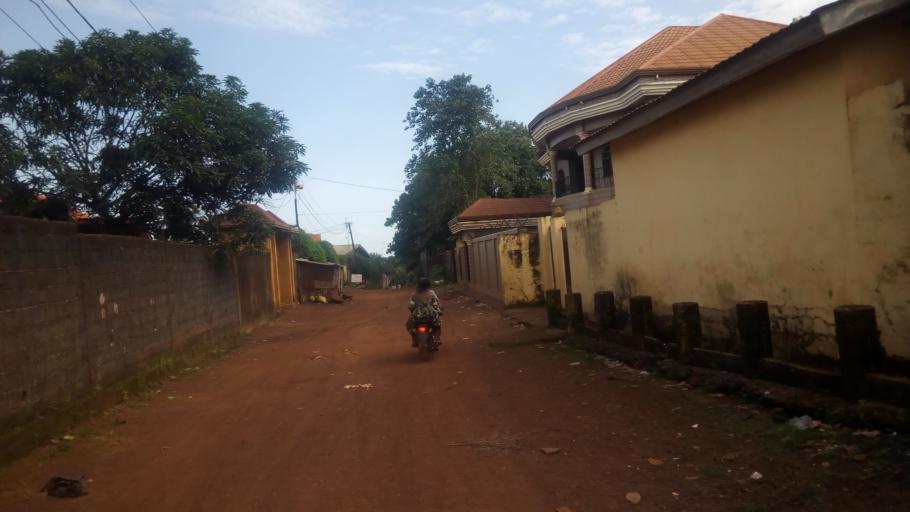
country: GN
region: Kindia
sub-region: Prefecture de Dubreka
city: Dubreka
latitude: 9.6506
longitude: -13.5344
